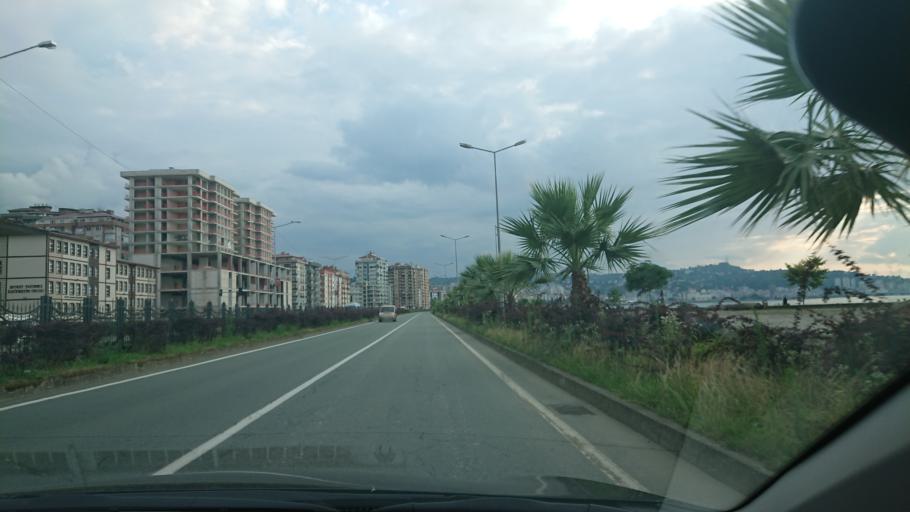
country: TR
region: Rize
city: Rize
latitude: 41.0290
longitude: 40.5485
